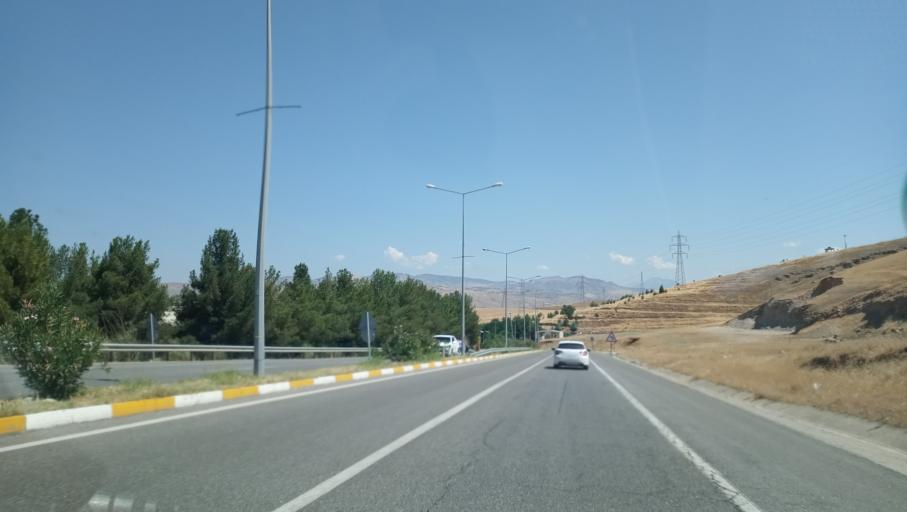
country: TR
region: Siirt
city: Civankan
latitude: 37.9514
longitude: 41.8624
